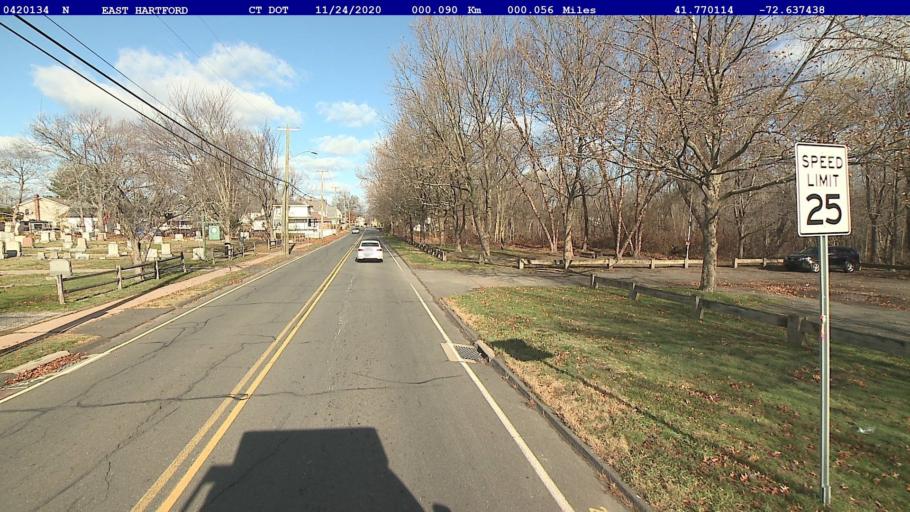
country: US
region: Connecticut
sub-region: Hartford County
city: East Hartford
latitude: 41.7701
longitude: -72.6374
